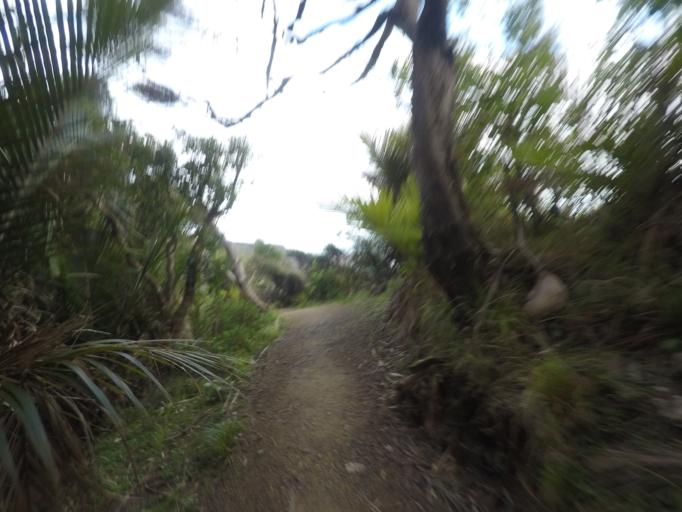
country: NZ
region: Auckland
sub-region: Auckland
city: Muriwai Beach
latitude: -36.9824
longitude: 174.4716
